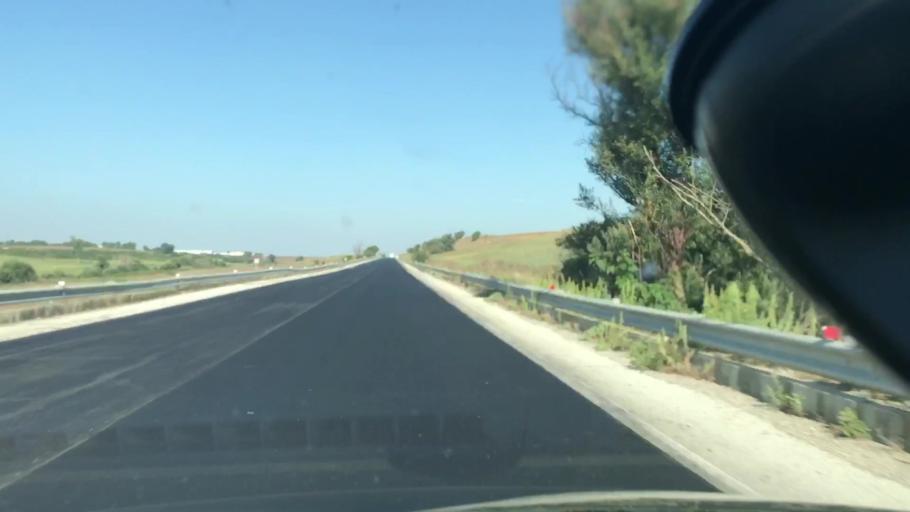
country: IT
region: Apulia
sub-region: Provincia di Barletta - Andria - Trani
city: Spinazzola
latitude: 40.9027
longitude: 16.1177
